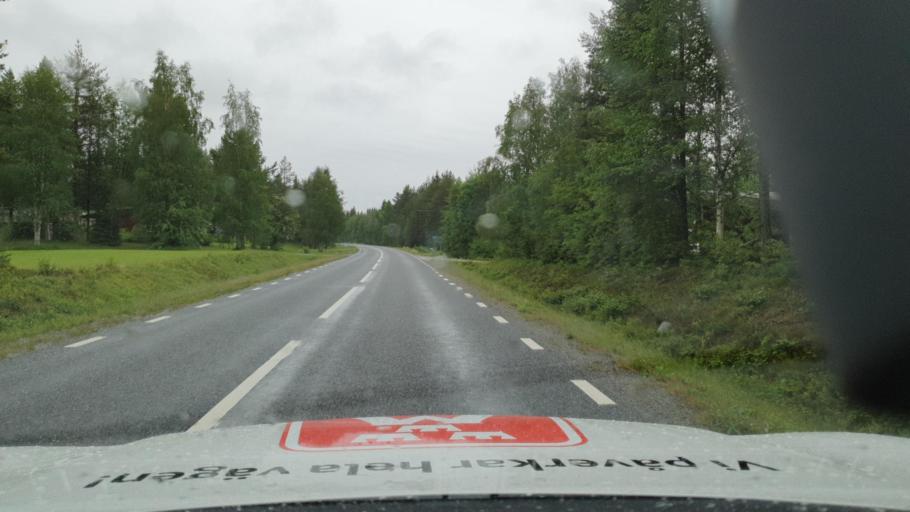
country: SE
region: Vaesterbotten
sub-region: Asele Kommun
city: Asele
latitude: 63.9977
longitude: 17.2653
